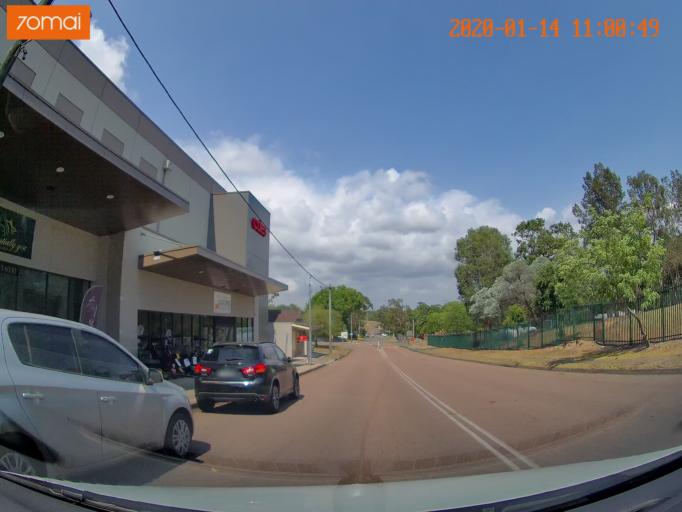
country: AU
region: New South Wales
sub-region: Lake Macquarie Shire
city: Dora Creek
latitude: -33.1063
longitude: 151.4875
